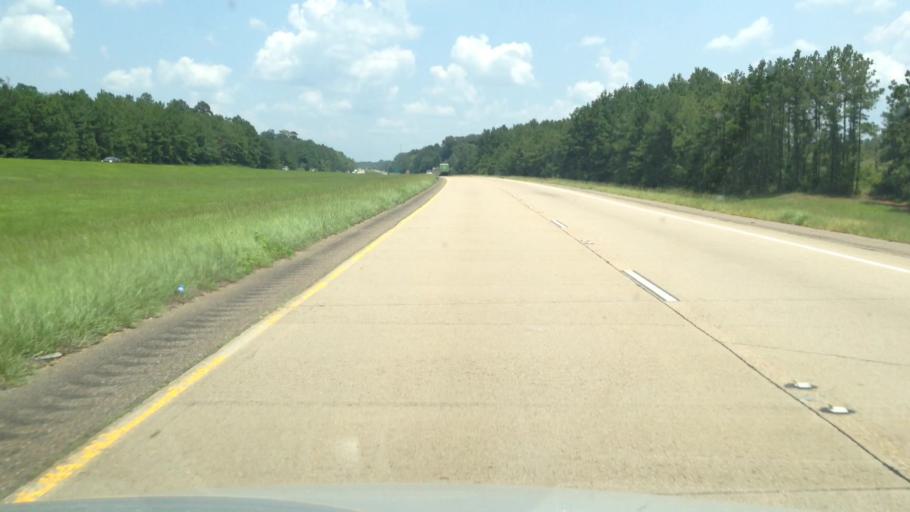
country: US
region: Louisiana
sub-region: Rapides Parish
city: Lecompte
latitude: 31.0286
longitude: -92.4058
